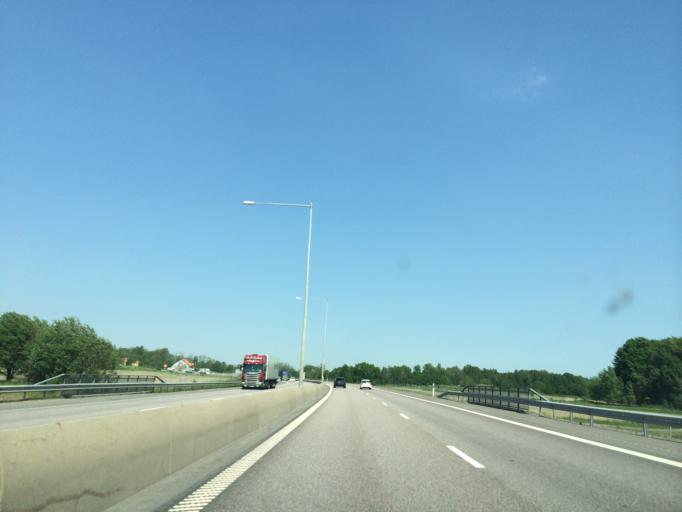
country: SE
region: OEstergoetland
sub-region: Norrkopings Kommun
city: Norrkoping
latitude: 58.5839
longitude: 16.1221
